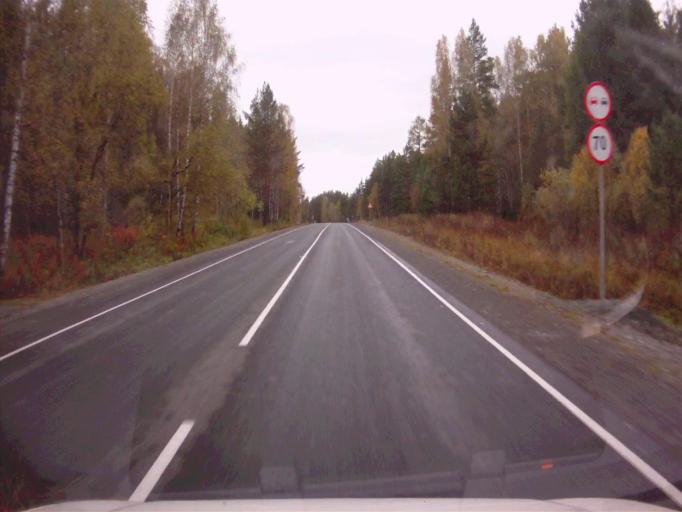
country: RU
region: Chelyabinsk
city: Nyazepetrovsk
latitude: 56.0593
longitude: 59.7320
